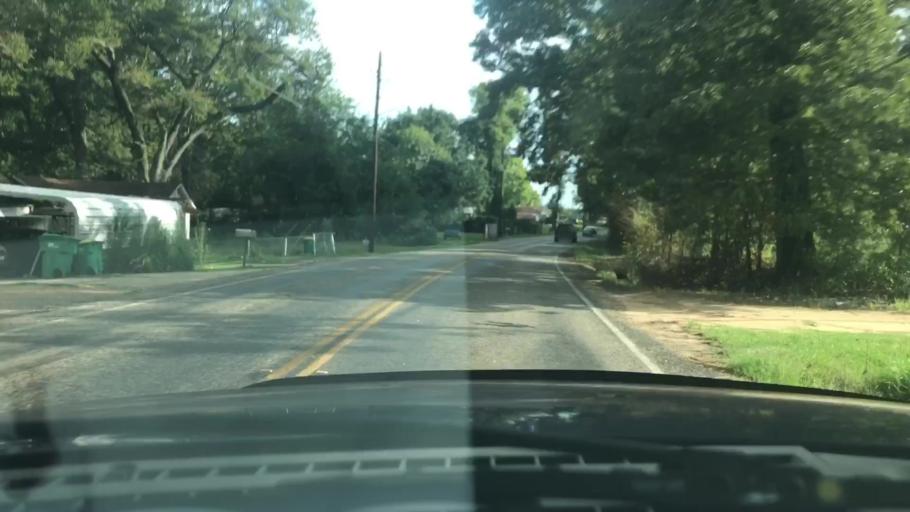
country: US
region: Texas
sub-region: Bowie County
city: Texarkana
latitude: 33.3991
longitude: -94.0639
